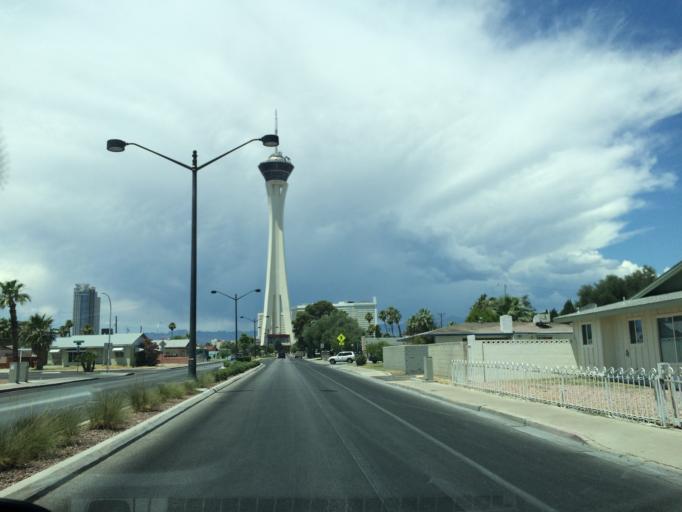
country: US
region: Nevada
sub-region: Clark County
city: Las Vegas
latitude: 36.1478
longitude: -115.1465
